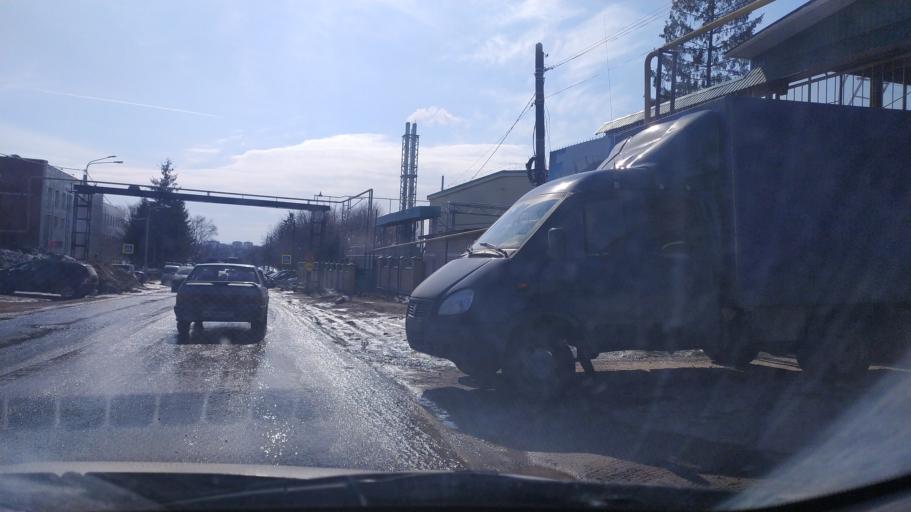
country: RU
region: Chuvashia
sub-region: Cheboksarskiy Rayon
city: Cheboksary
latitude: 56.1194
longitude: 47.2902
